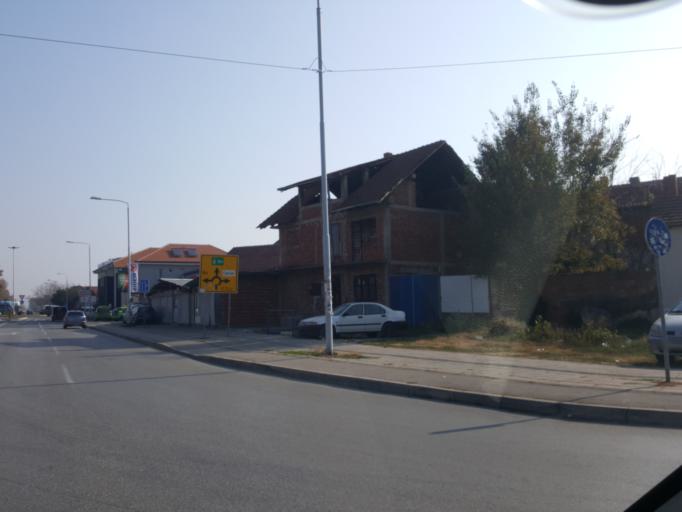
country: RS
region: Central Serbia
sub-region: Jablanicki Okrug
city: Leskovac
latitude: 43.0035
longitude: 21.9346
